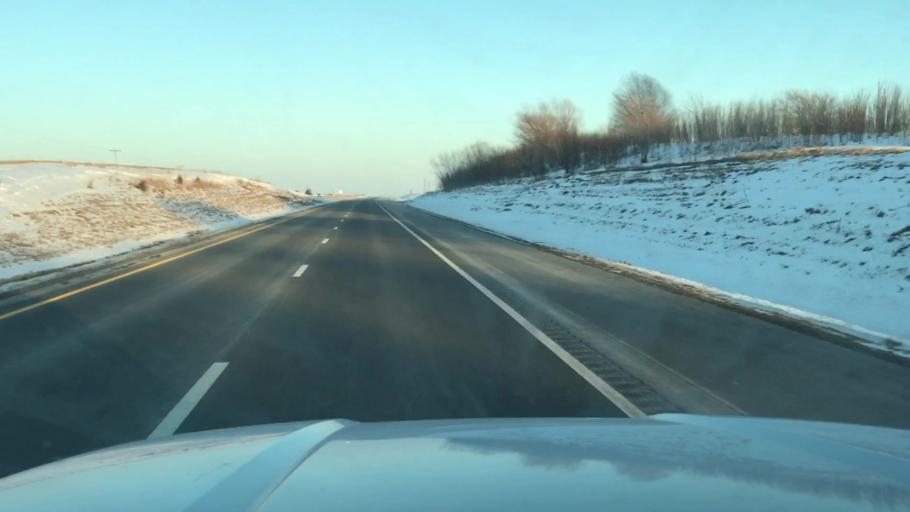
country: US
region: Missouri
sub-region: Clinton County
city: Gower
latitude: 39.7620
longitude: -94.5297
